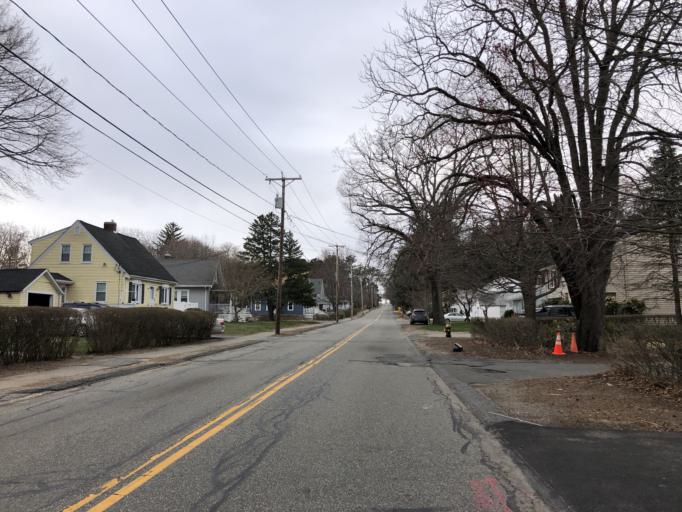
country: US
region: Massachusetts
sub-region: Norfolk County
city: Stoughton
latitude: 42.1225
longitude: -71.0896
